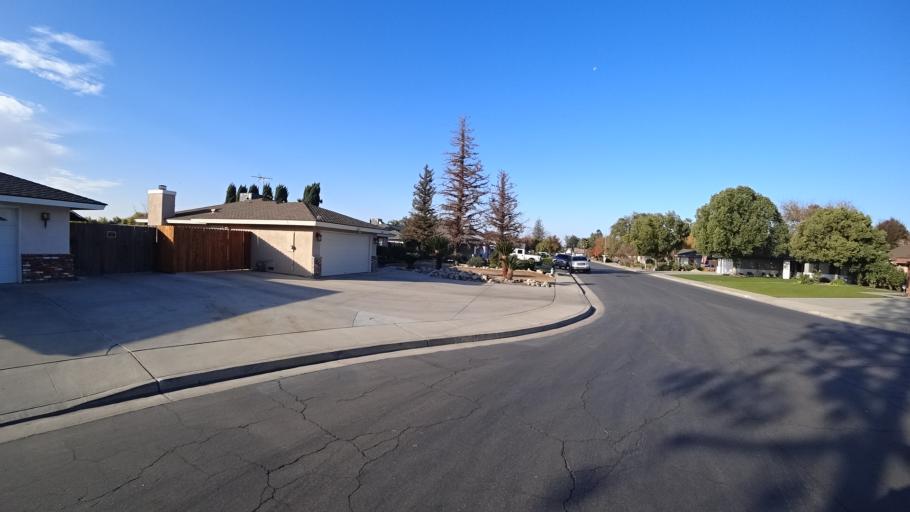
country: US
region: California
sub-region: Kern County
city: Rosedale
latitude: 35.3477
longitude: -119.1502
